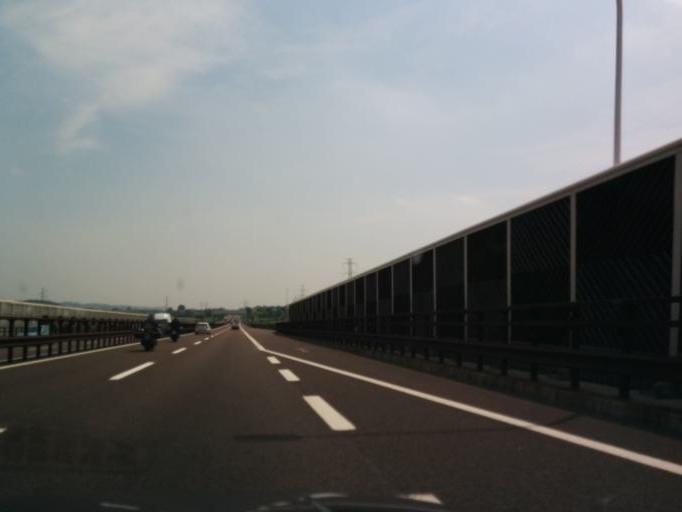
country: IT
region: Veneto
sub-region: Provincia di Verona
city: Cavajon Veronese
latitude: 45.5360
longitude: 10.7799
